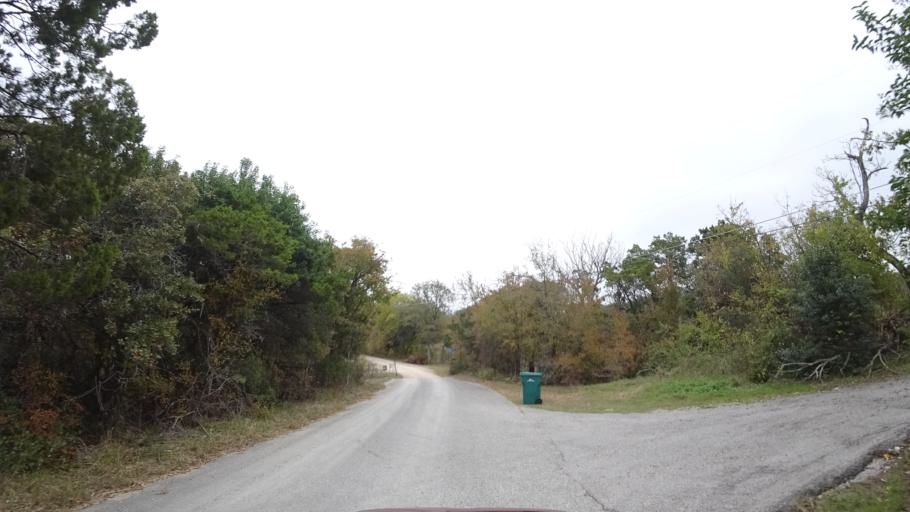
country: US
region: Texas
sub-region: Williamson County
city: Anderson Mill
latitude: 30.4454
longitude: -97.8372
